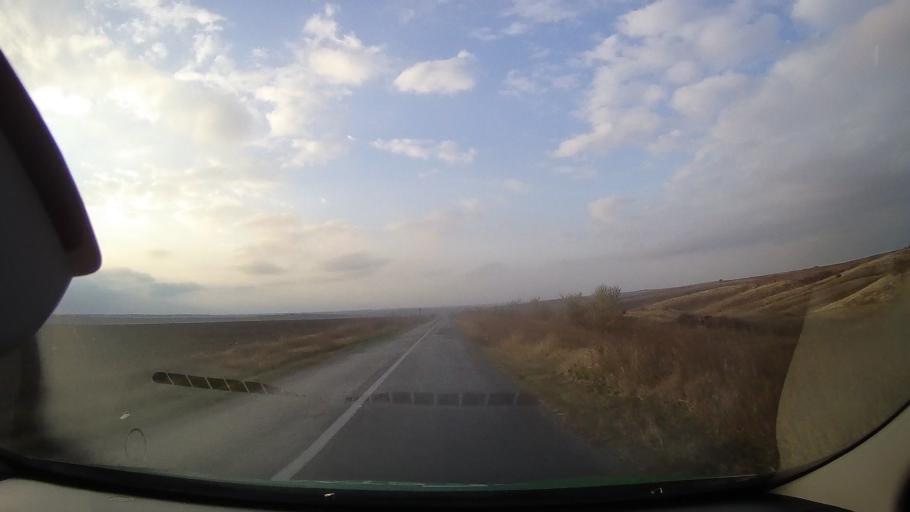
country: RO
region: Constanta
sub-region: Comuna Adamclisi
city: Adamclisi
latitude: 44.0171
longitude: 27.8921
